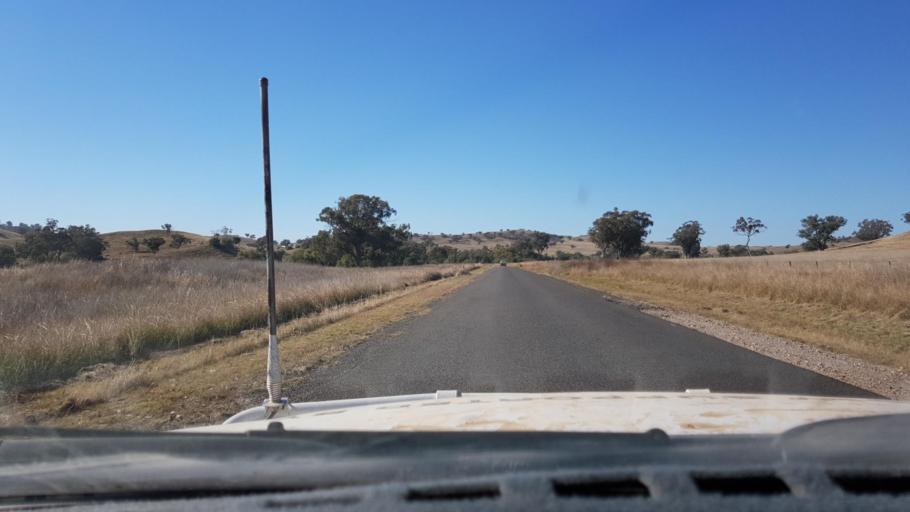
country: AU
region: New South Wales
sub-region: Narrabri
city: Blair Athol
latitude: -30.6705
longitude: 150.3832
